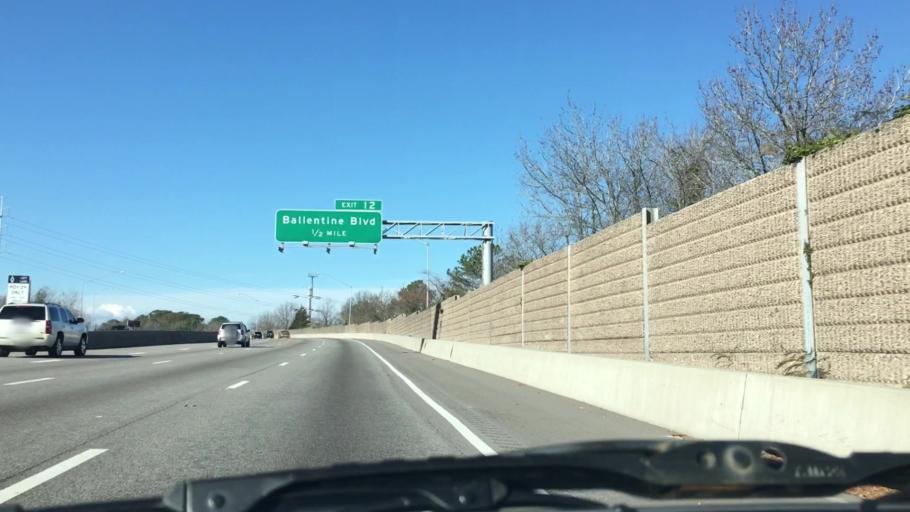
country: US
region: Virginia
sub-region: City of Chesapeake
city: Chesapeake
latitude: 36.8451
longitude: -76.2409
